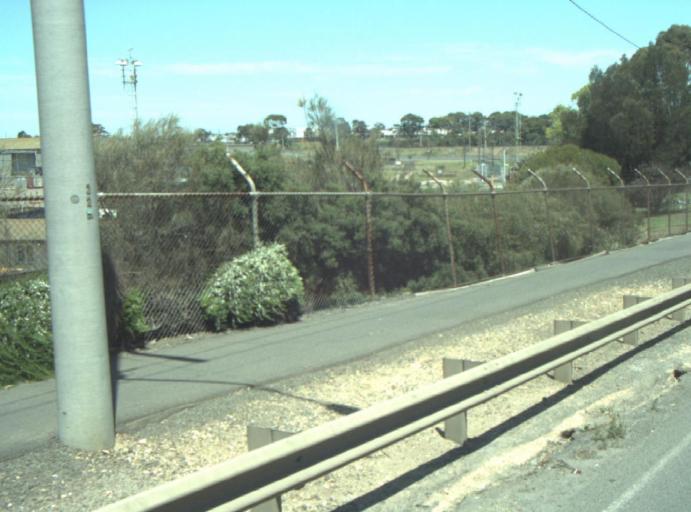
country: AU
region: Victoria
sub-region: Greater Geelong
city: Bell Park
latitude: -38.1039
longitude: 144.3621
